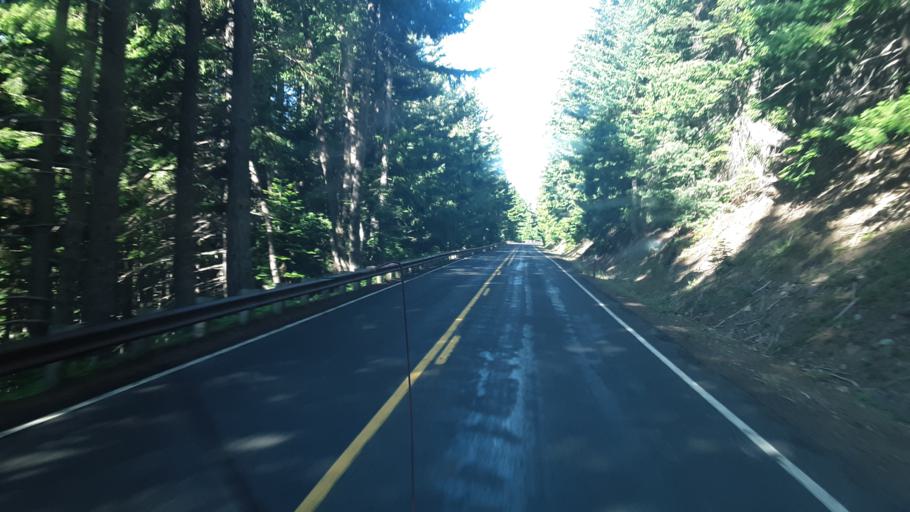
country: US
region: Washington
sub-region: Kittitas County
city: Cle Elum
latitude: 46.9002
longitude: -121.4384
